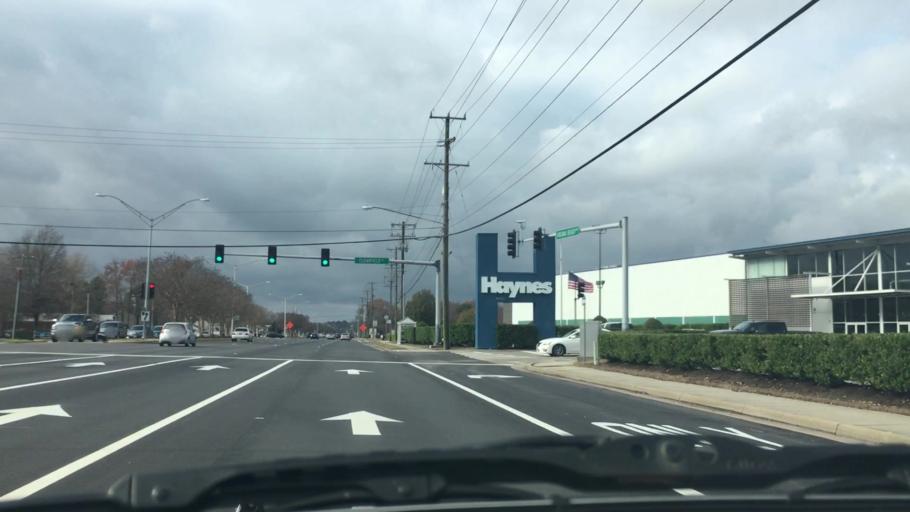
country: US
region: Virginia
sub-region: City of Chesapeake
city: Chesapeake
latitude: 36.8489
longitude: -76.1639
